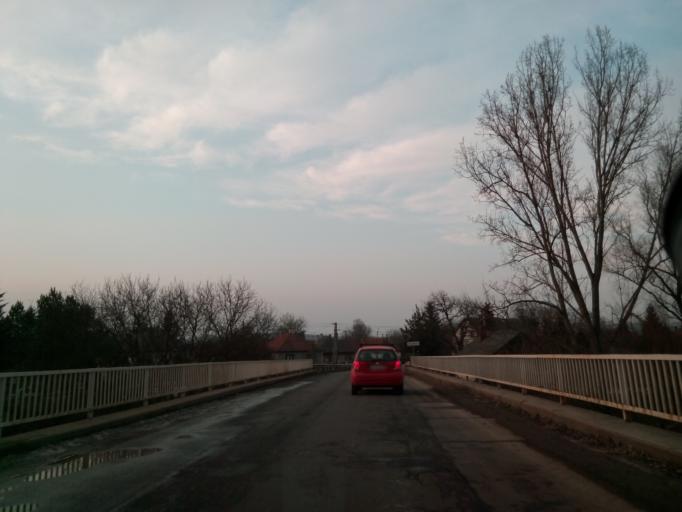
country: HU
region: Borsod-Abauj-Zemplen
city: Gonc
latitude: 48.4977
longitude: 21.2304
